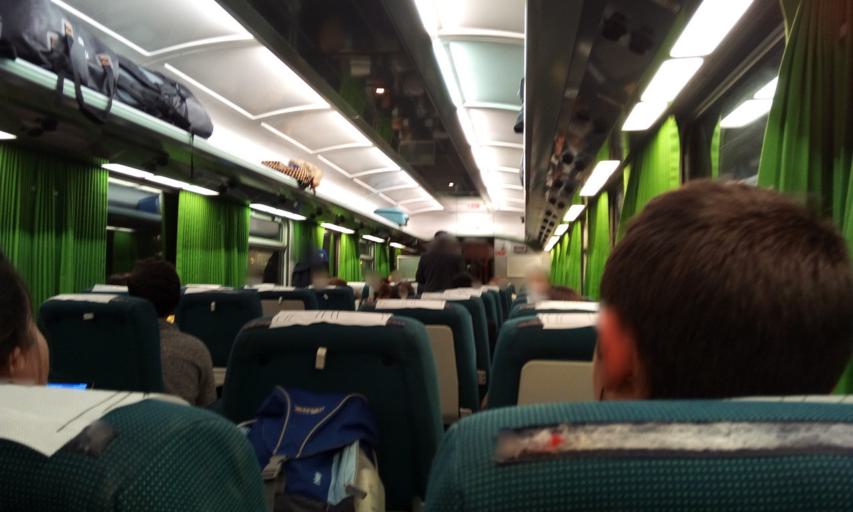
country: PT
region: Santarem
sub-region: Entroncamento
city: Entroncamento
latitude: 39.4685
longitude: -8.4673
